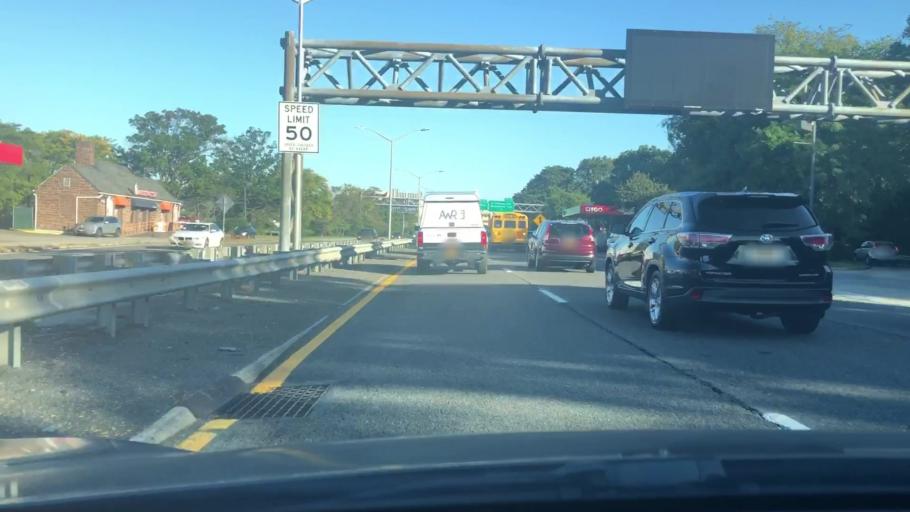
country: US
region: New York
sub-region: Bronx
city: The Bronx
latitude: 40.8357
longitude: -73.8385
